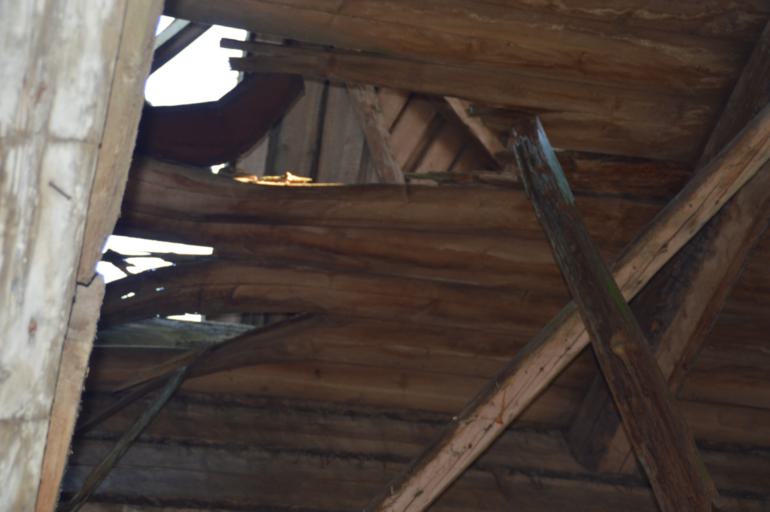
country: RU
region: Kirov
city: Sozimskiy
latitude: 59.9466
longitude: 52.4184
